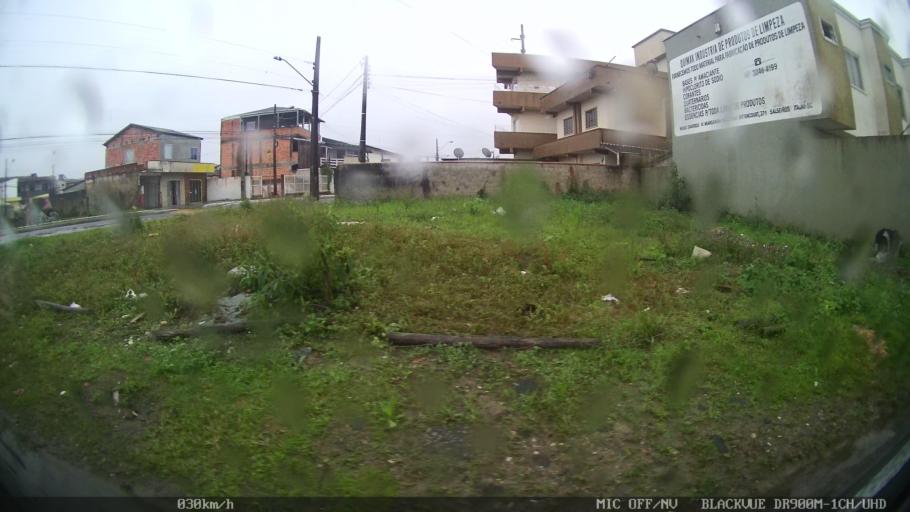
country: BR
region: Santa Catarina
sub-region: Itajai
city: Itajai
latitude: -26.9271
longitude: -48.6940
